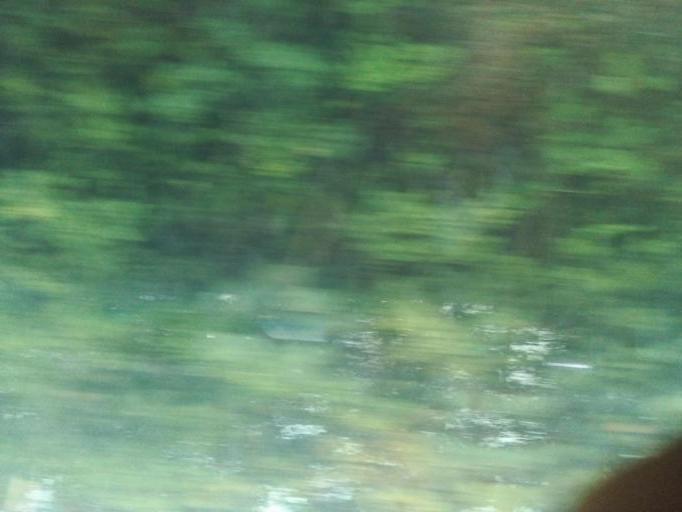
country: BR
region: Maranhao
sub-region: Imperatriz
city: Imperatriz
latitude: -4.9288
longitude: -47.4268
